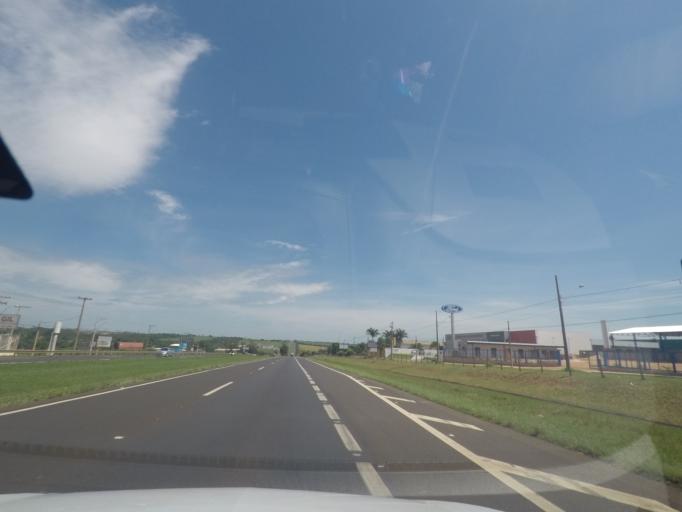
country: BR
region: Sao Paulo
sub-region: Araraquara
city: Araraquara
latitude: -21.7805
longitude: -48.2282
